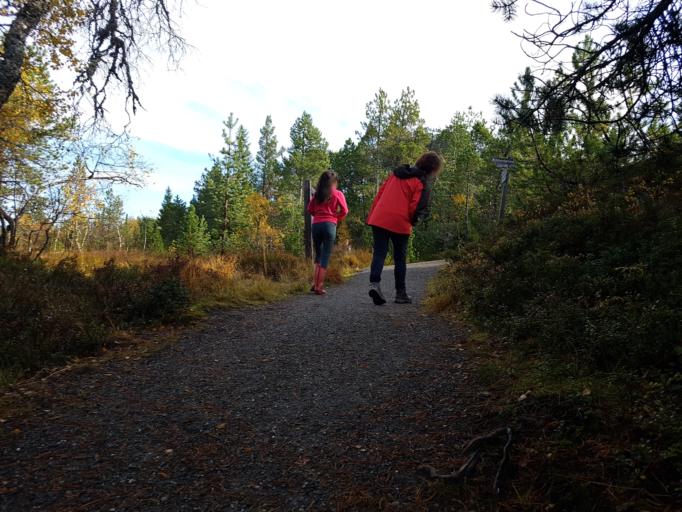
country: NO
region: Sor-Trondelag
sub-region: Trondheim
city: Trondheim
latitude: 63.4276
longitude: 10.2817
